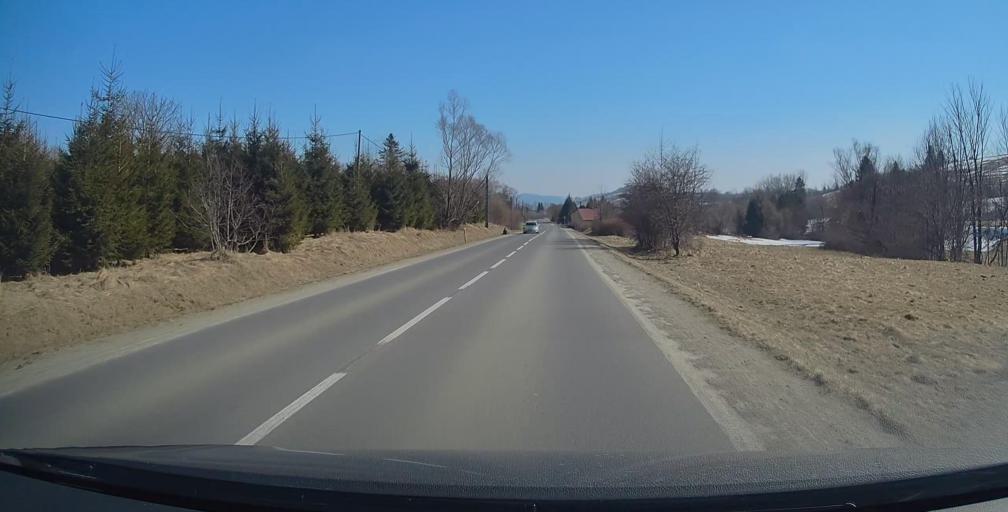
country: PL
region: Subcarpathian Voivodeship
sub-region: Powiat bieszczadzki
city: Ustrzyki Dolne
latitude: 49.5094
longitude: 22.6165
